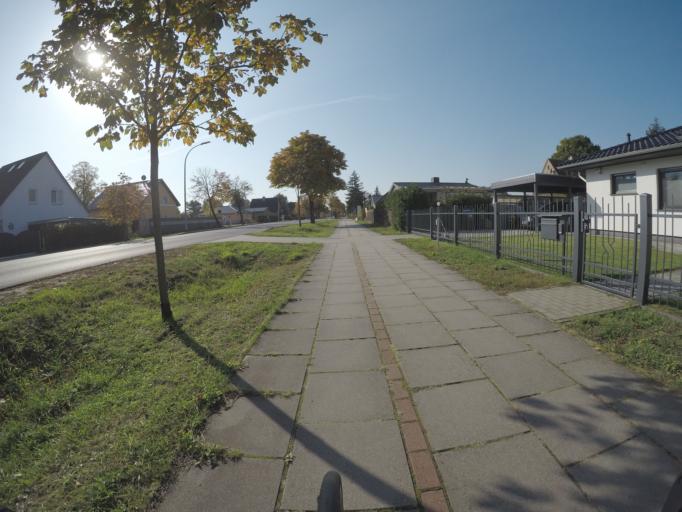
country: DE
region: Brandenburg
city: Oranienburg
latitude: 52.7359
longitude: 13.2466
